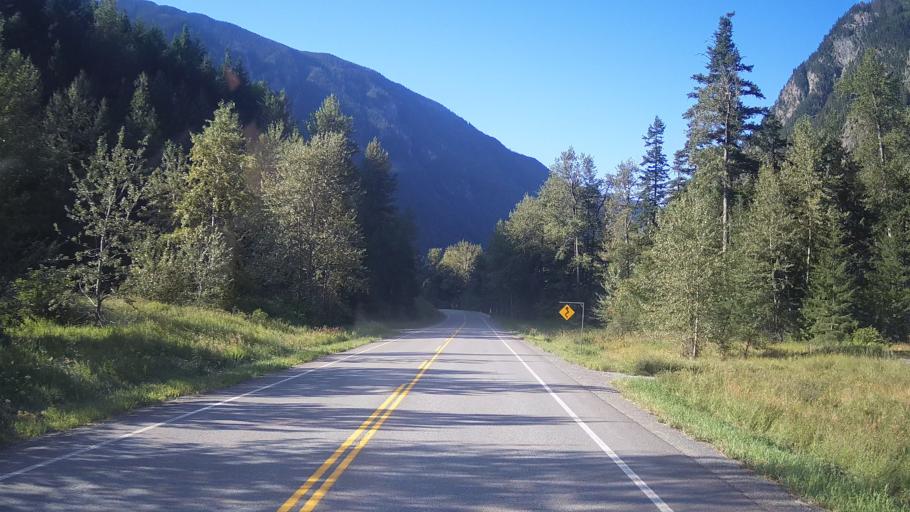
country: CA
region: British Columbia
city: Lillooet
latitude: 50.5761
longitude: -122.0882
